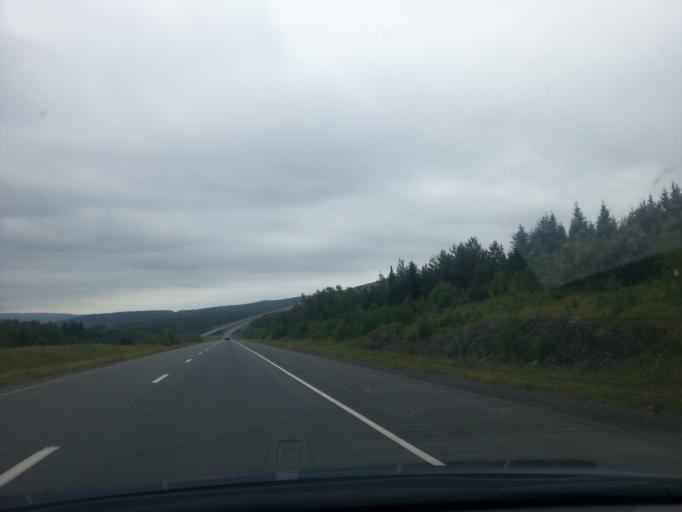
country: CA
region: New Brunswick
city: Nackawic
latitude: 45.9960
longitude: -67.5122
